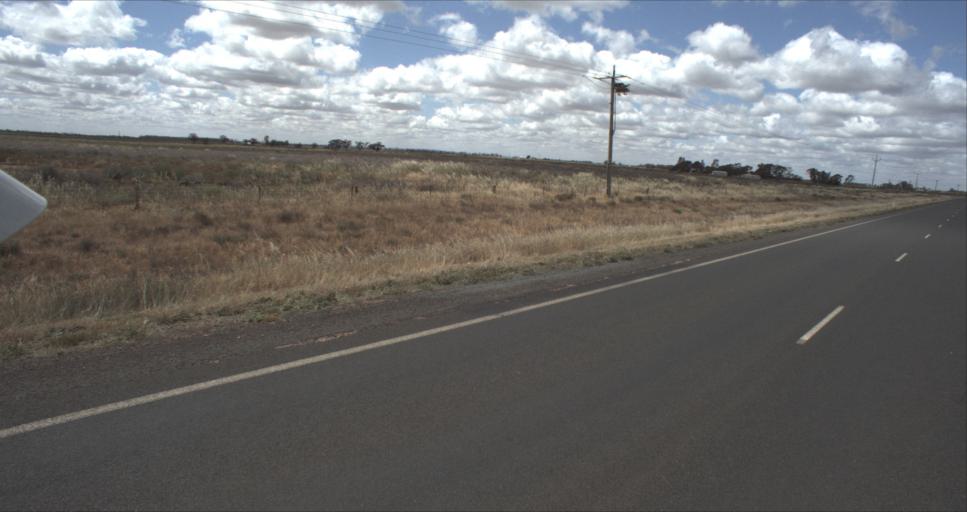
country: AU
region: New South Wales
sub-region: Murrumbidgee Shire
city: Darlington Point
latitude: -34.4906
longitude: 146.1644
